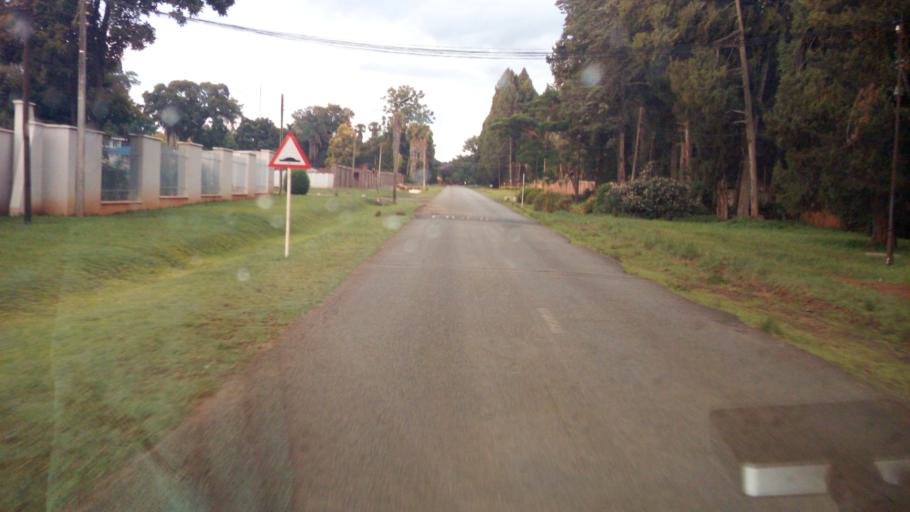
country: ZW
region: Harare
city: Harare
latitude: -17.7806
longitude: 31.0995
